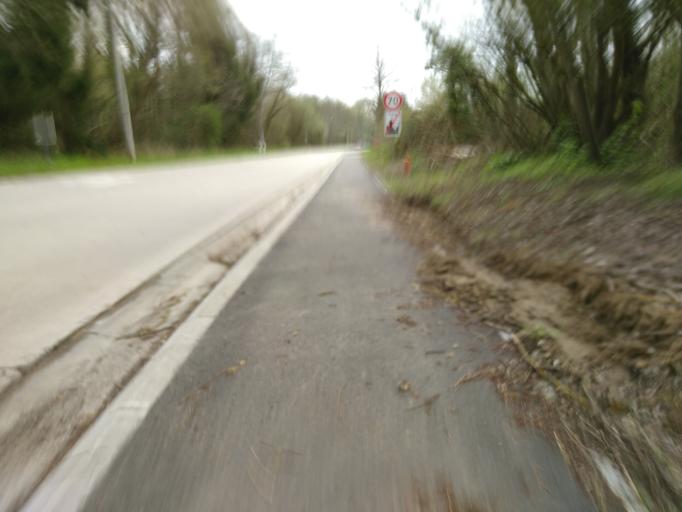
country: BE
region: Wallonia
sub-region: Province du Brabant Wallon
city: Chaumont-Gistoux
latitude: 50.6820
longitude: 4.6935
